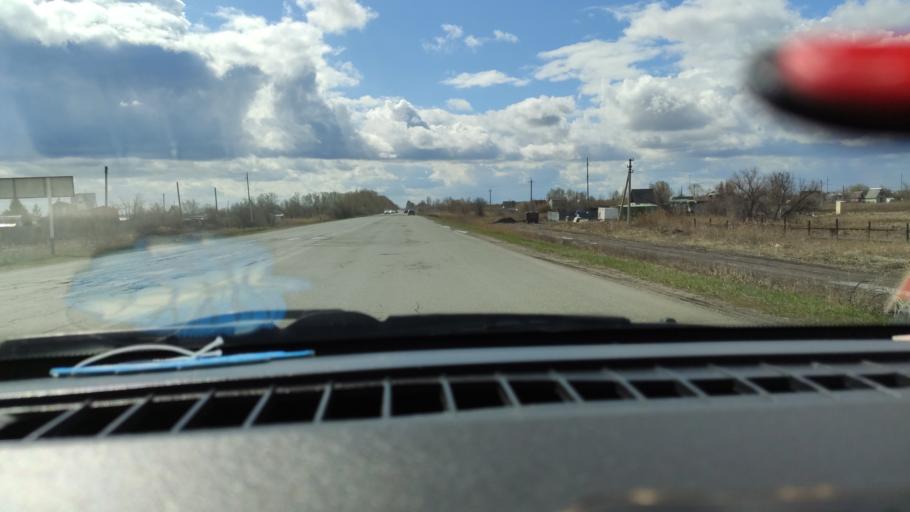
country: RU
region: Samara
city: Tol'yatti
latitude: 53.7082
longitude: 49.4227
